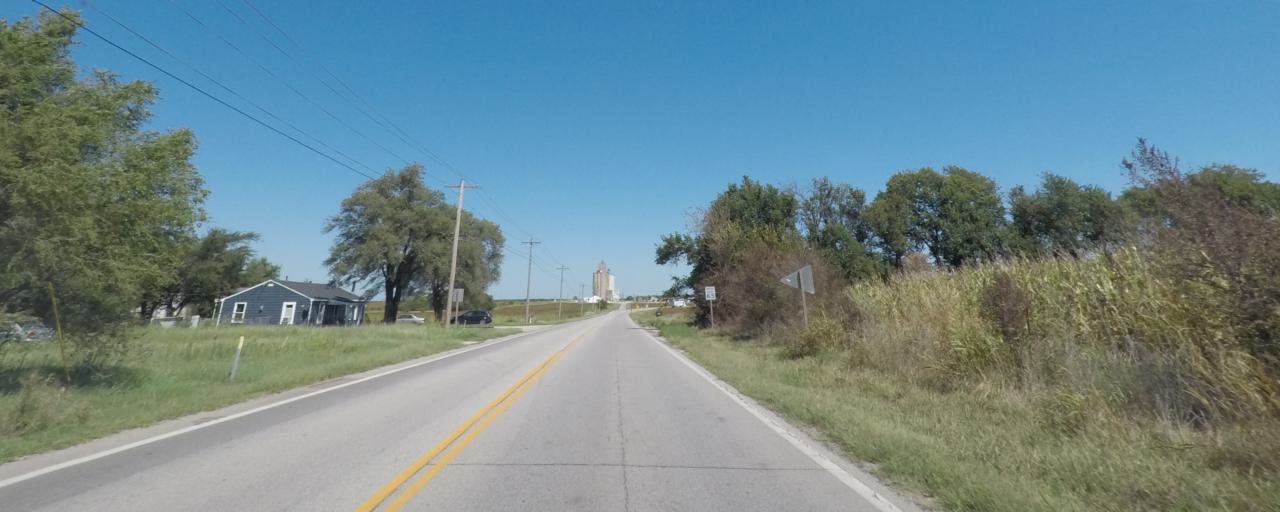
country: US
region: Kansas
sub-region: Sumner County
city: Wellington
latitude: 37.2965
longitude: -97.3939
